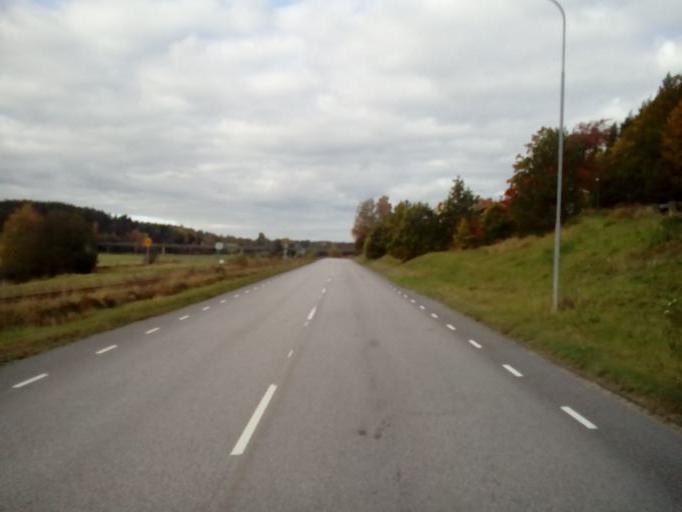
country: SE
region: Kalmar
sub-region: Vasterviks Kommun
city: Gamleby
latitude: 57.9048
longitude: 16.3956
